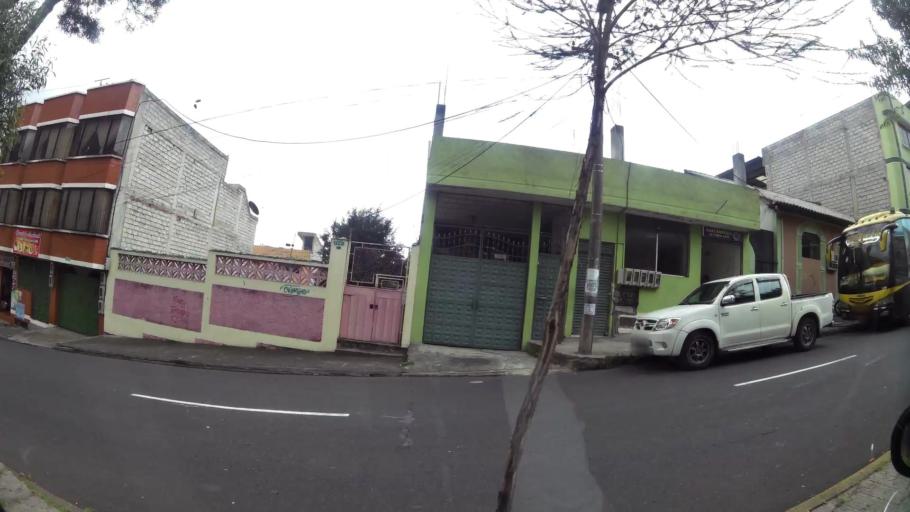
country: EC
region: Pichincha
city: Quito
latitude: -0.2465
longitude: -78.5094
